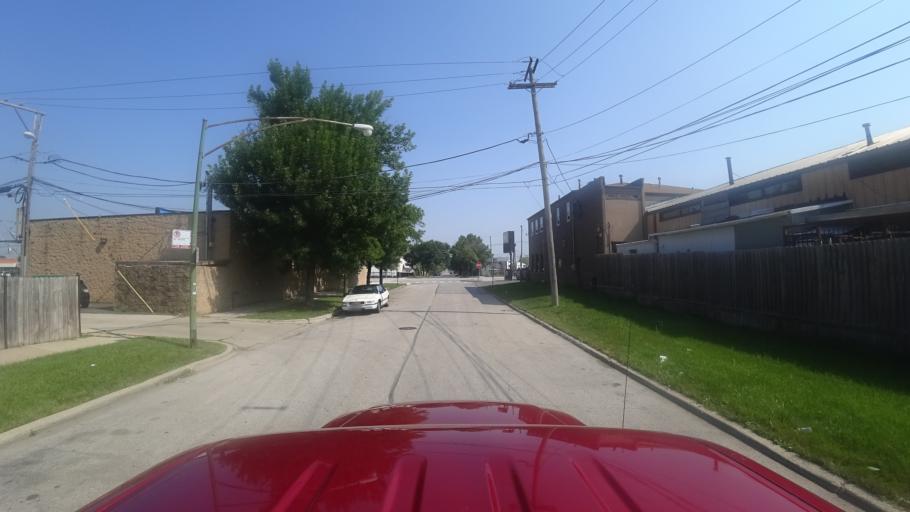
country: US
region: Illinois
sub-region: Cook County
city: Stickney
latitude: 41.7986
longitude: -87.7393
